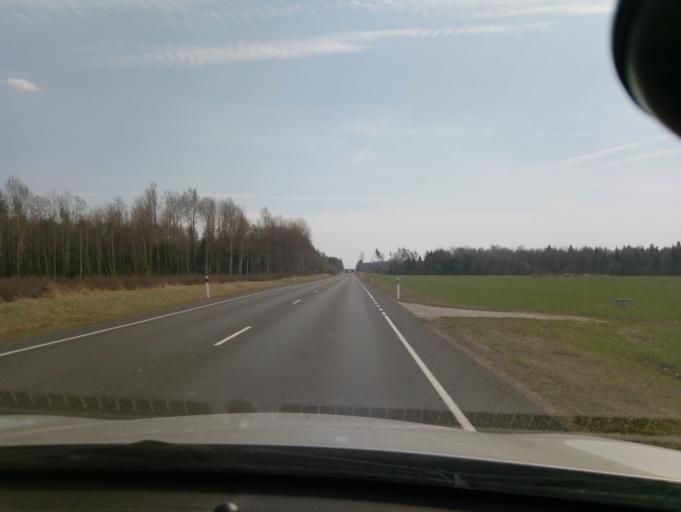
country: EE
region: Viljandimaa
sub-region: Vohma linn
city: Vohma
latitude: 58.7234
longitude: 25.6026
